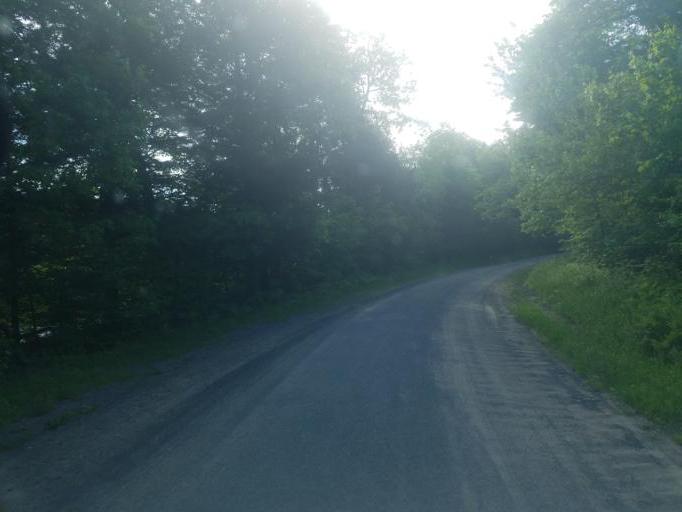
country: US
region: New York
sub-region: Herkimer County
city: Dolgeville
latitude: 43.3758
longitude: -74.9150
